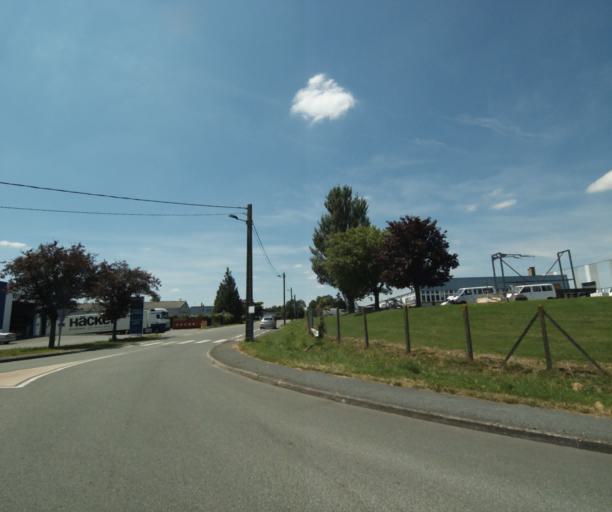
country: FR
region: Pays de la Loire
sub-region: Departement de la Mayenne
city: Laval
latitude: 48.0856
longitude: -0.7477
